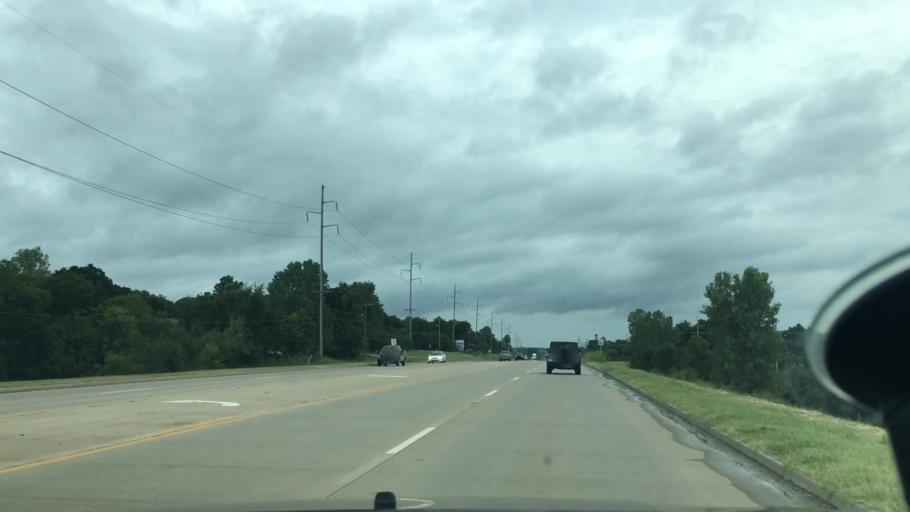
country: US
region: Oklahoma
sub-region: Seminole County
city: Seminole
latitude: 35.2548
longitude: -96.6712
